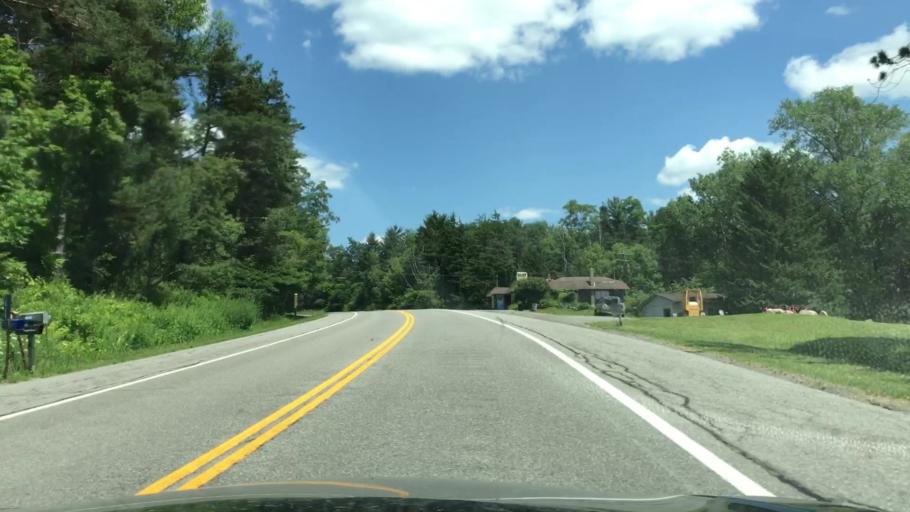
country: US
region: New York
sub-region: Erie County
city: East Aurora
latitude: 42.7649
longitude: -78.5100
